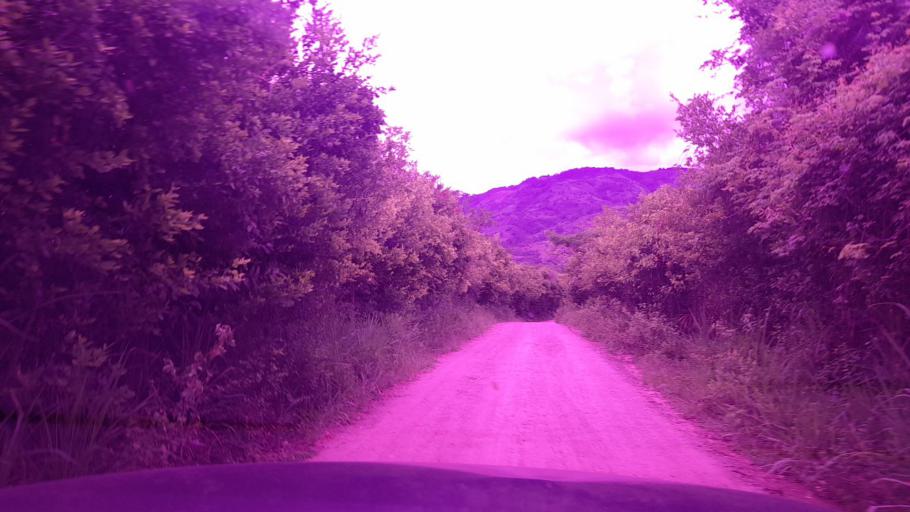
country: CO
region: Valle del Cauca
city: Bugalagrande
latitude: 4.1709
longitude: -76.0787
